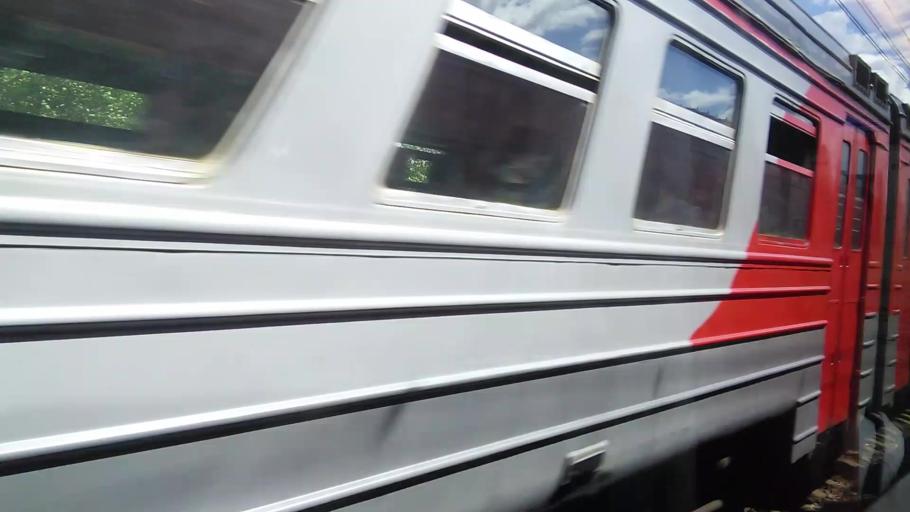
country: RU
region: Moscow
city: Likhobory
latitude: 55.8505
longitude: 37.5730
